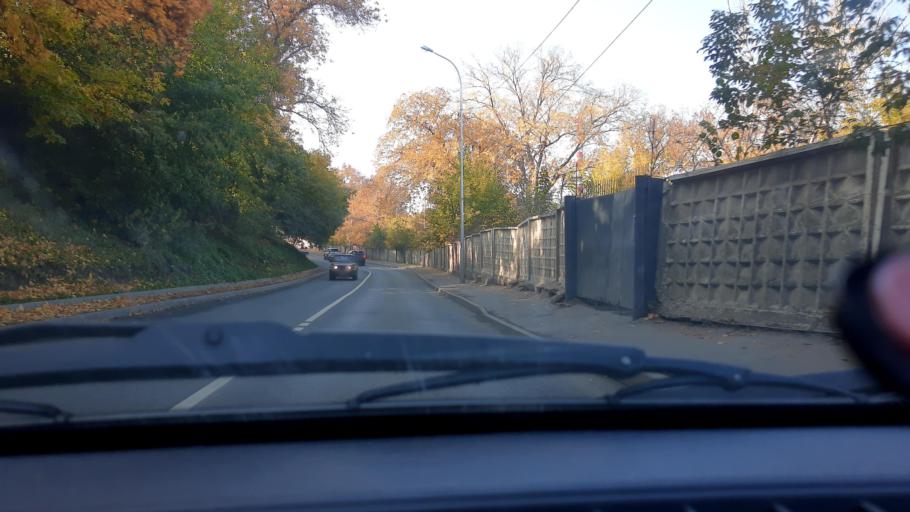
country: RU
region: Bashkortostan
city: Ufa
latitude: 54.7495
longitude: 55.9559
